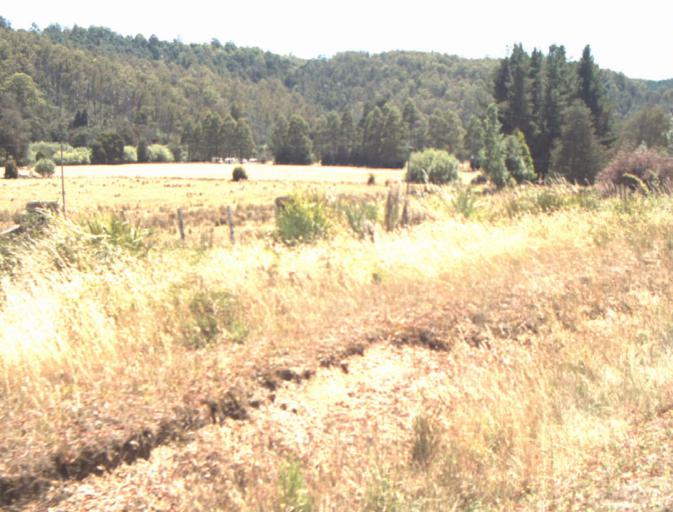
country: AU
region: Tasmania
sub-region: Dorset
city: Scottsdale
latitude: -41.3160
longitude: 147.3668
